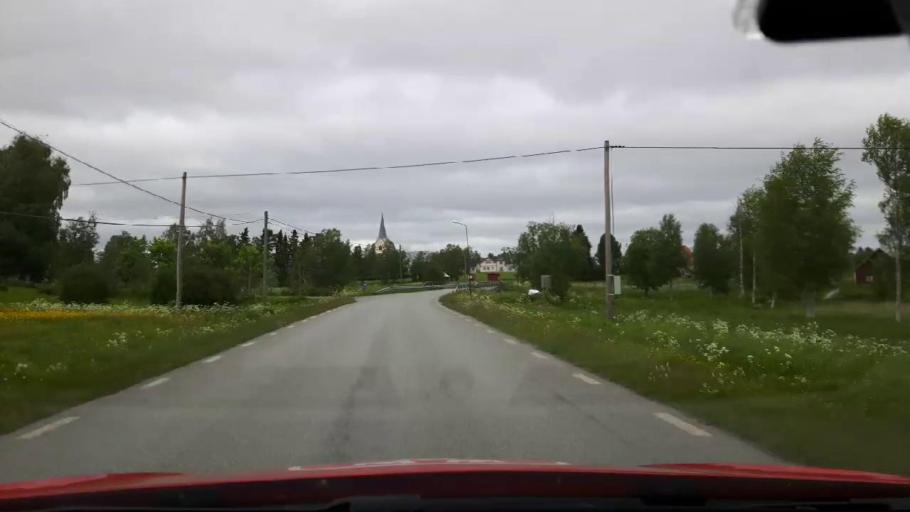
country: SE
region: Jaemtland
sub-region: OEstersunds Kommun
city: Lit
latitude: 63.6714
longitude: 15.1011
